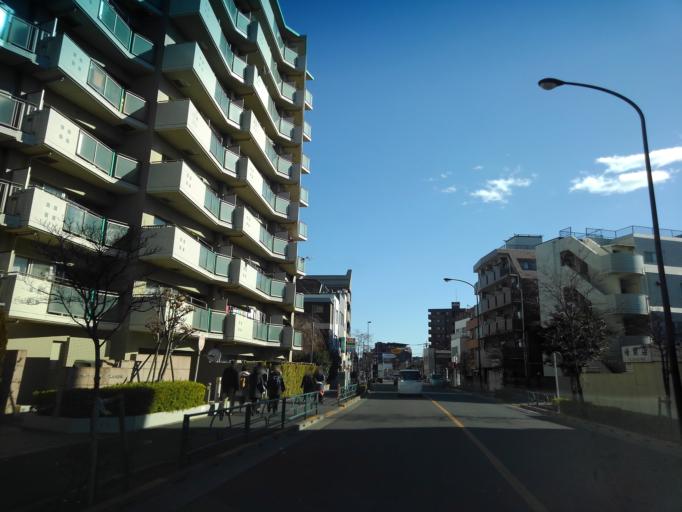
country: JP
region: Tokyo
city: Chofugaoka
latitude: 35.6471
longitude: 139.5609
